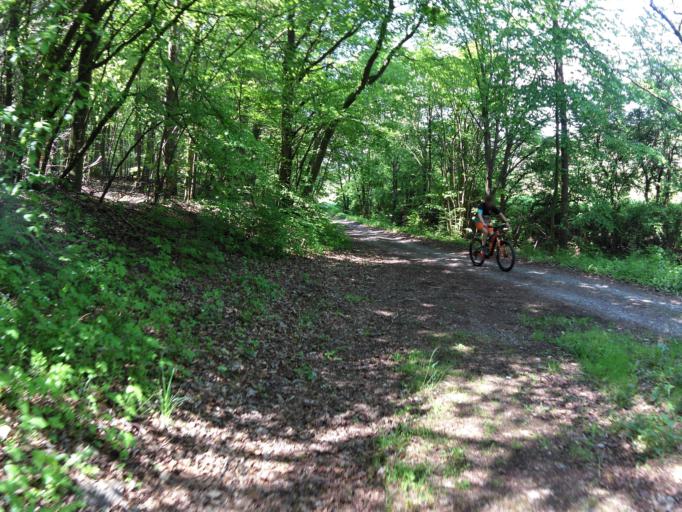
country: DE
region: Bavaria
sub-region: Regierungsbezirk Unterfranken
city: Eibelstadt
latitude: 49.7401
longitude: 10.0110
